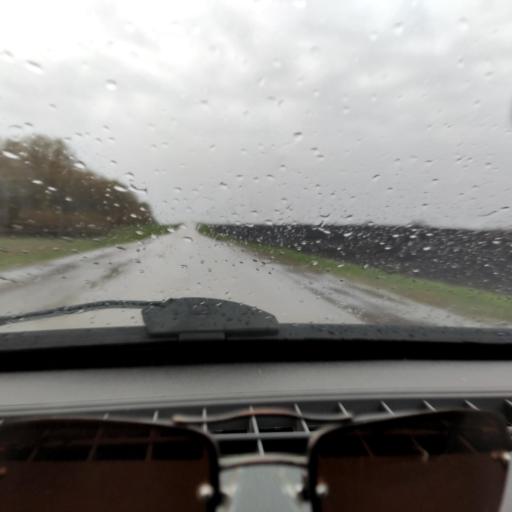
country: RU
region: Bashkortostan
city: Ulukulevo
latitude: 54.4554
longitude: 56.2483
